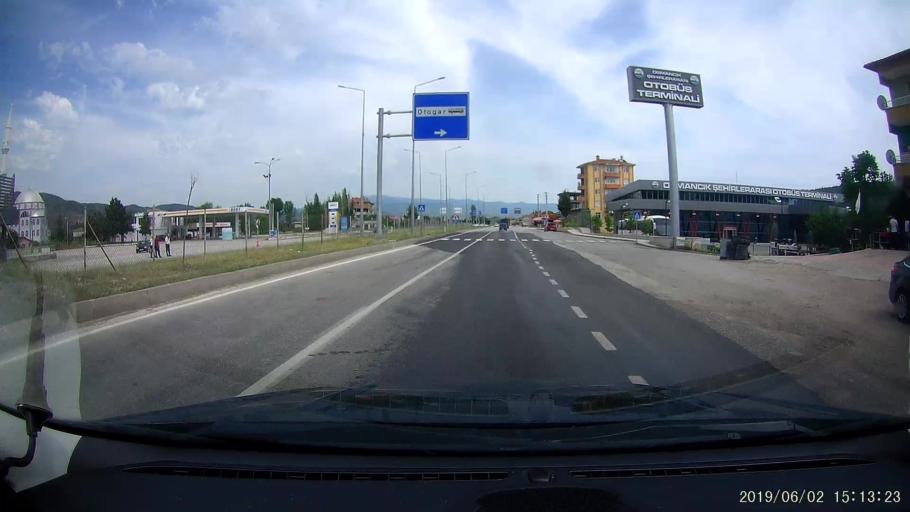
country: TR
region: Corum
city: Osmancik
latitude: 40.9725
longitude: 34.8208
